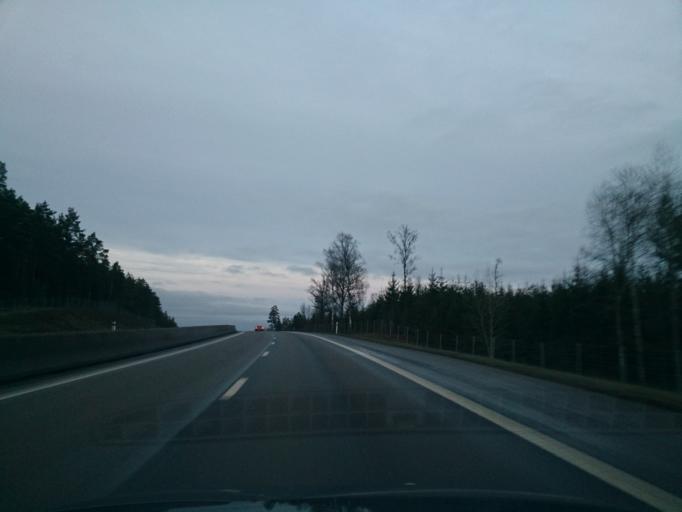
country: SE
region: OEstergoetland
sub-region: Norrkopings Kommun
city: Kimstad
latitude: 58.5351
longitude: 16.0377
